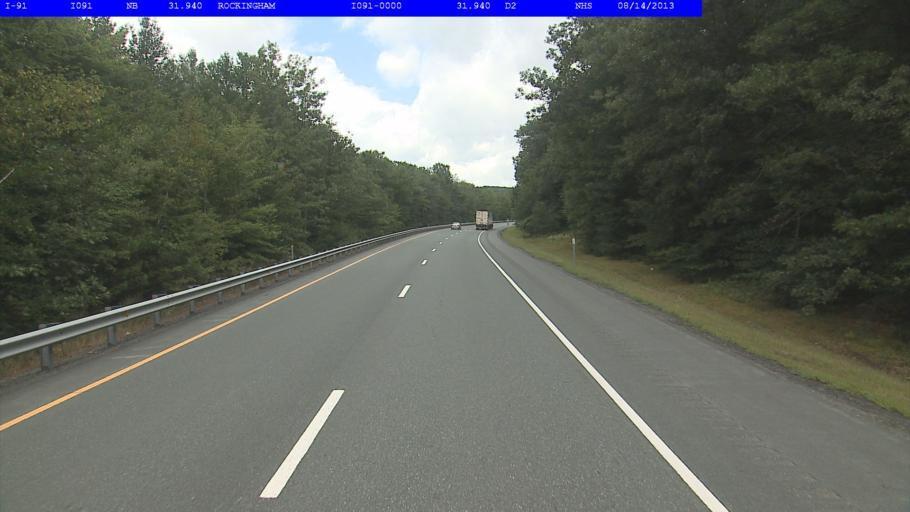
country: US
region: Vermont
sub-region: Windham County
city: Bellows Falls
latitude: 43.1347
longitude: -72.4755
